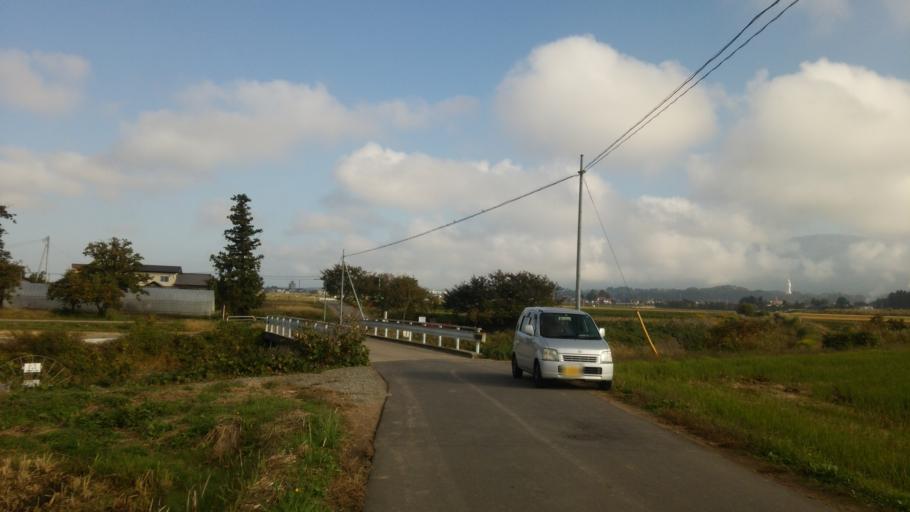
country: JP
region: Fukushima
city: Kitakata
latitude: 37.5319
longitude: 139.9356
